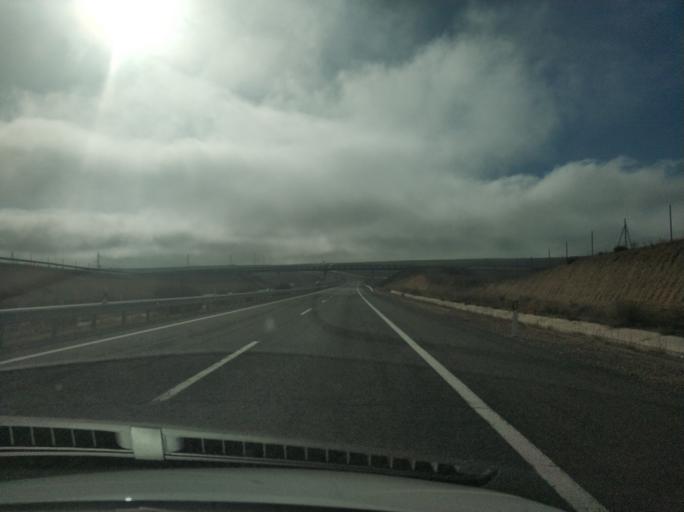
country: ES
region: Castille and Leon
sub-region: Provincia de Soria
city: Alcubilla de las Penas
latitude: 41.2870
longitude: -2.4762
